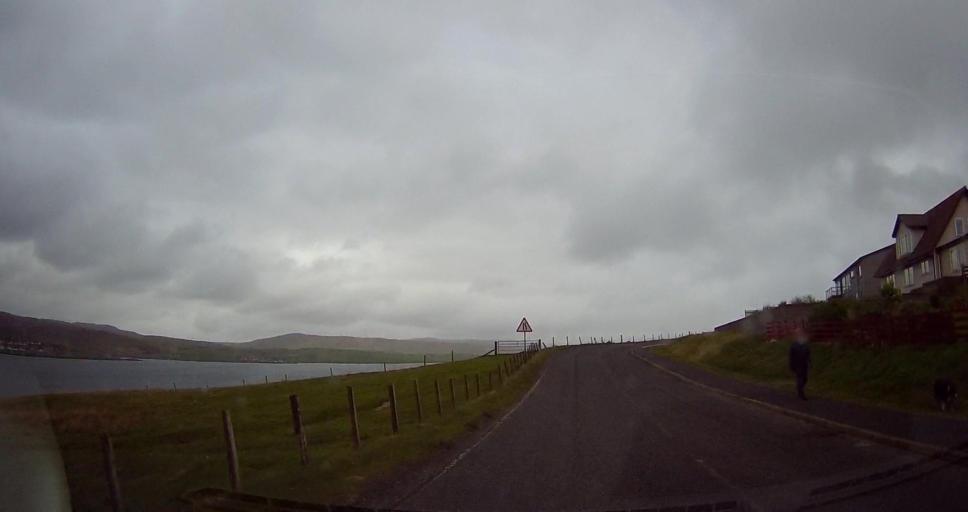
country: GB
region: Scotland
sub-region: Shetland Islands
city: Lerwick
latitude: 60.3911
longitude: -1.3697
